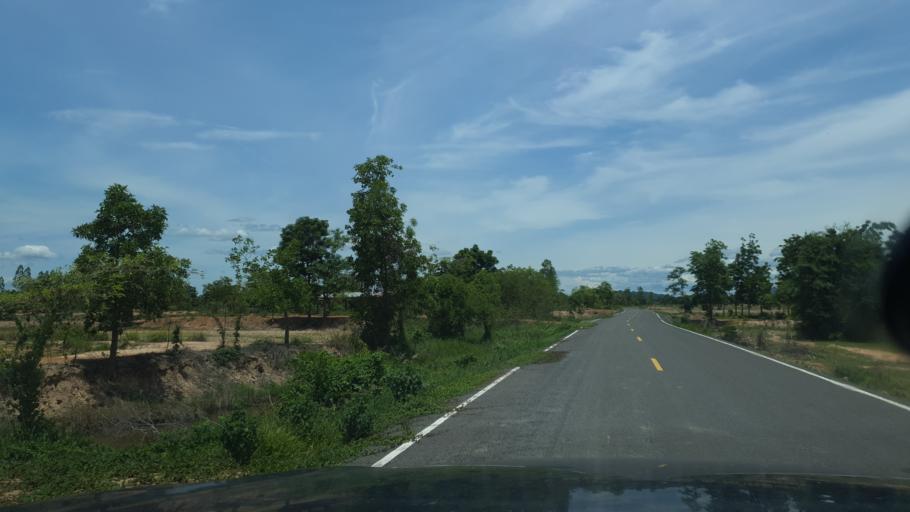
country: TH
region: Sukhothai
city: Ban Na
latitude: 17.1507
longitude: 99.6515
